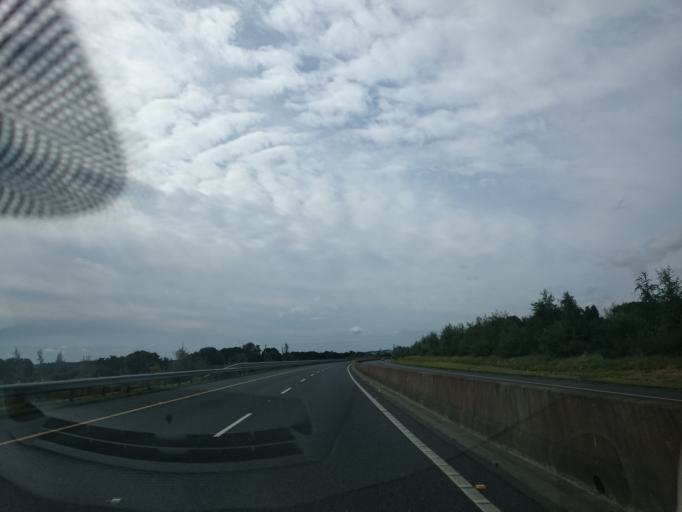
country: IE
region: Munster
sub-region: Waterford
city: Waterford
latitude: 52.3099
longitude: -7.1409
